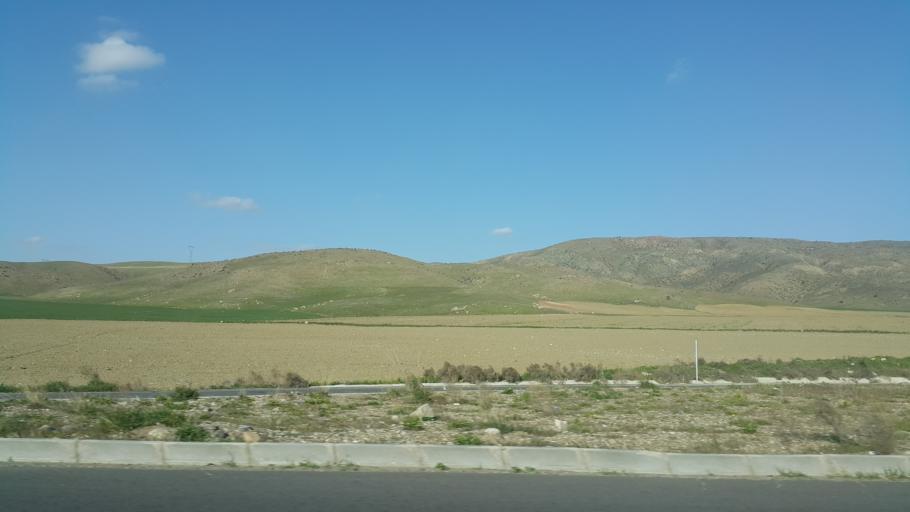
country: TR
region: Ankara
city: Sereflikochisar
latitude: 38.8285
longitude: 33.5962
